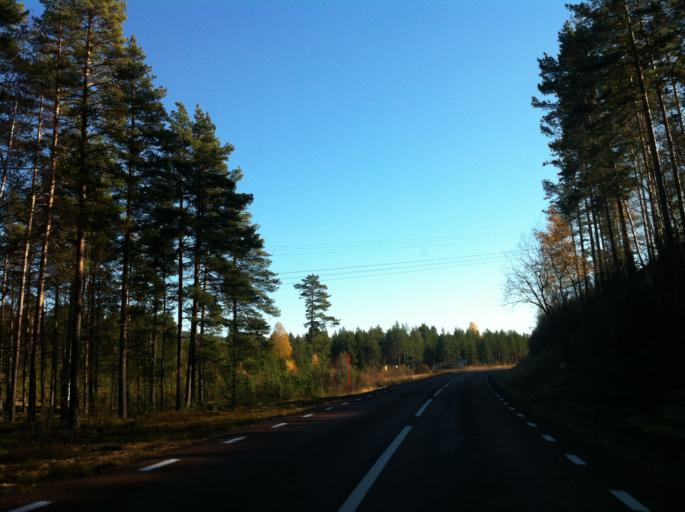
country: SE
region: Dalarna
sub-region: Alvdalens Kommun
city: AElvdalen
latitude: 61.3129
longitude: 13.6794
